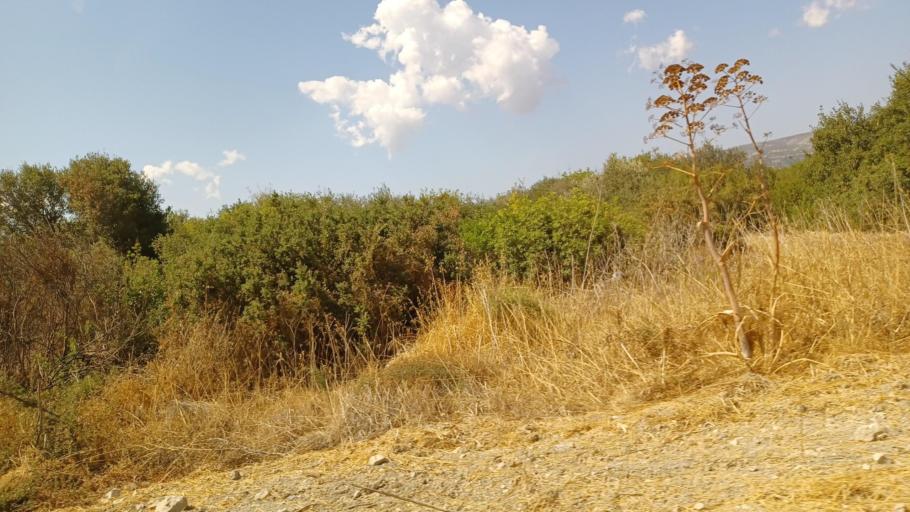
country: CY
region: Pafos
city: Polis
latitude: 34.9770
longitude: 32.4897
